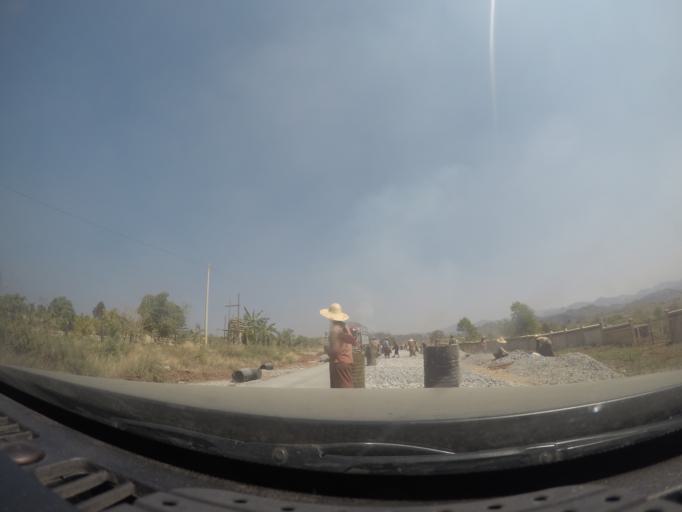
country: MM
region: Shan
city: Taunggyi
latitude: 20.8136
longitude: 97.2080
